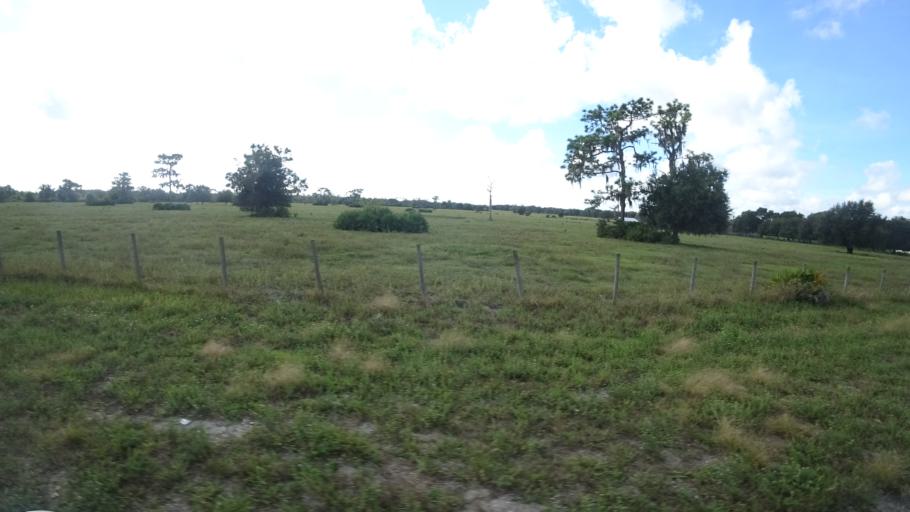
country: US
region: Florida
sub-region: Sarasota County
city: Lake Sarasota
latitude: 27.3392
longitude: -82.1972
